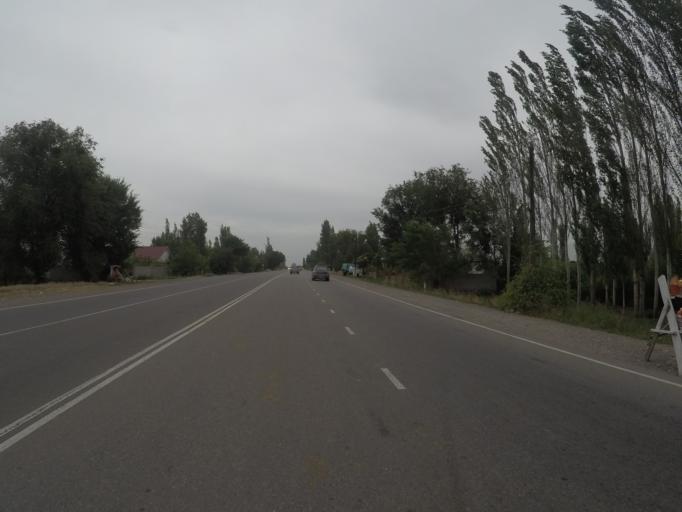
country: KG
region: Chuy
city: Bystrovka
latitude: 42.8221
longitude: 75.5630
